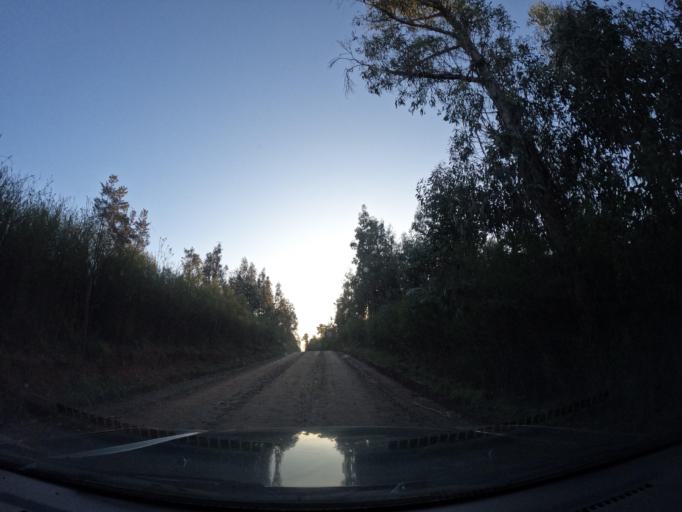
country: CL
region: Biobio
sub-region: Provincia de Concepcion
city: Chiguayante
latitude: -37.0116
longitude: -72.8813
